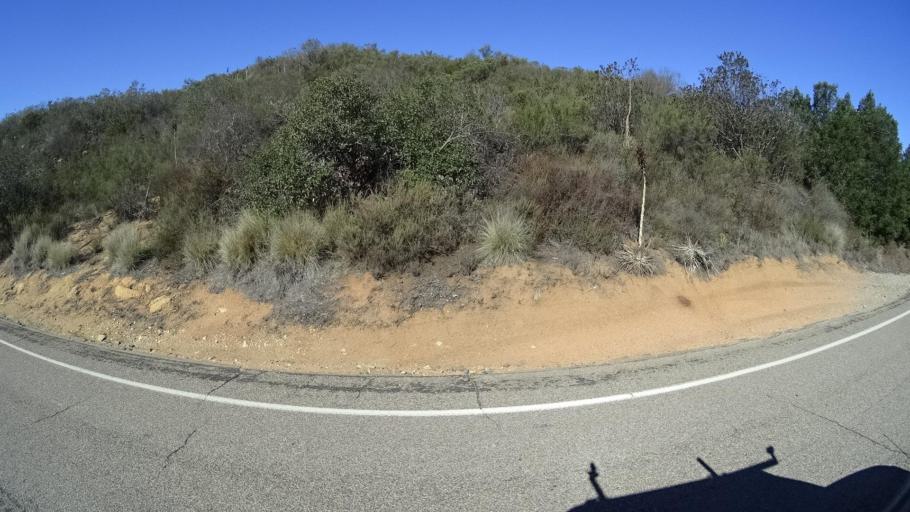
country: US
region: California
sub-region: San Diego County
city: Jamul
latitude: 32.7316
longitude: -116.8200
